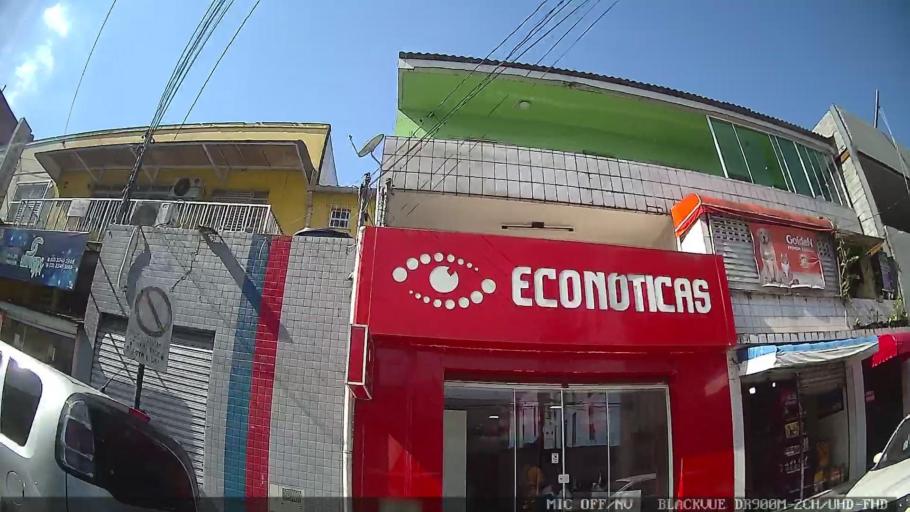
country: BR
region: Sao Paulo
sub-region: Santos
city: Santos
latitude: -23.9422
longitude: -46.3039
